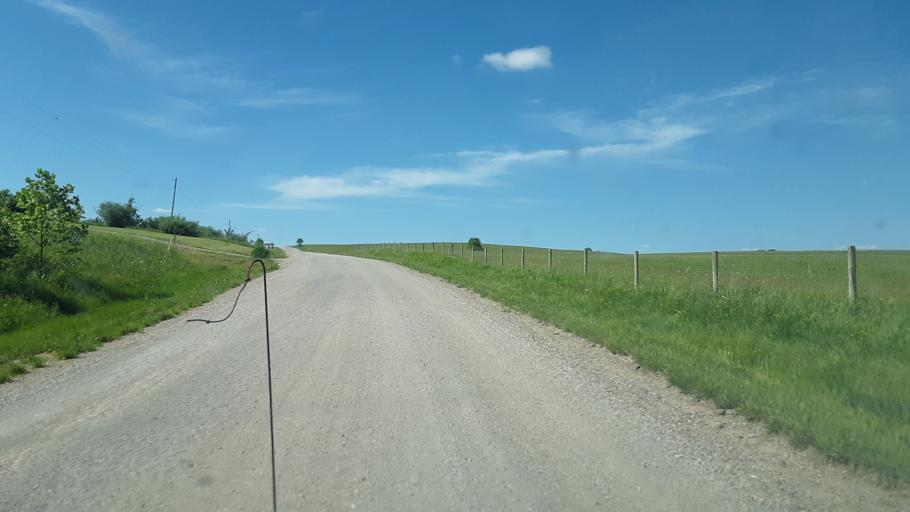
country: US
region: Ohio
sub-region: Tuscarawas County
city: Newcomerstown
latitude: 40.2381
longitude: -81.6722
